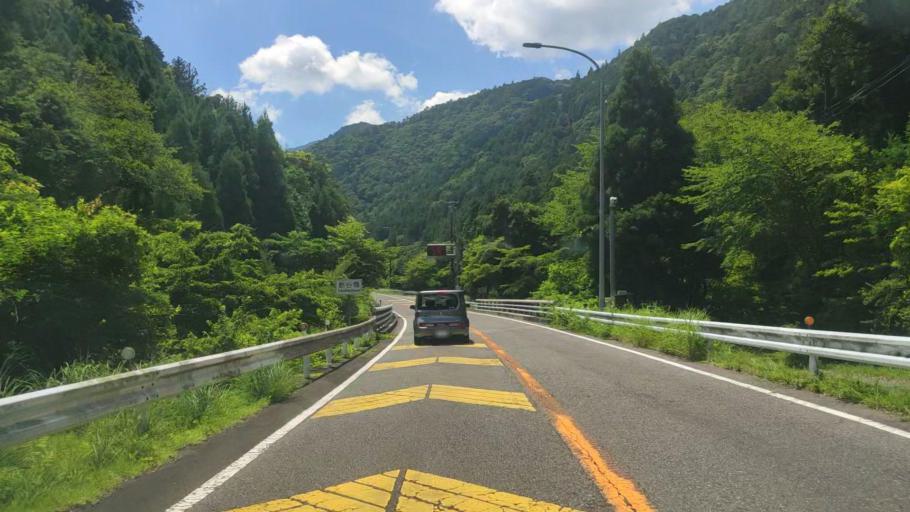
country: JP
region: Mie
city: Owase
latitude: 33.9921
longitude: 136.1187
